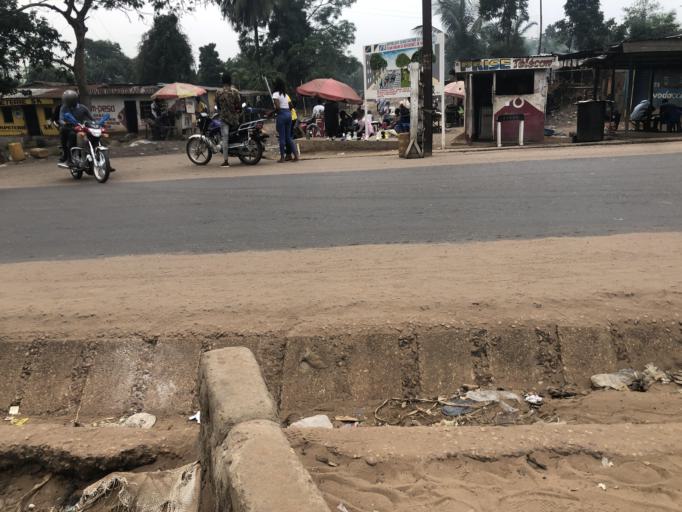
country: CD
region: Bandundu
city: Kikwit
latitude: -5.0548
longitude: 18.8012
